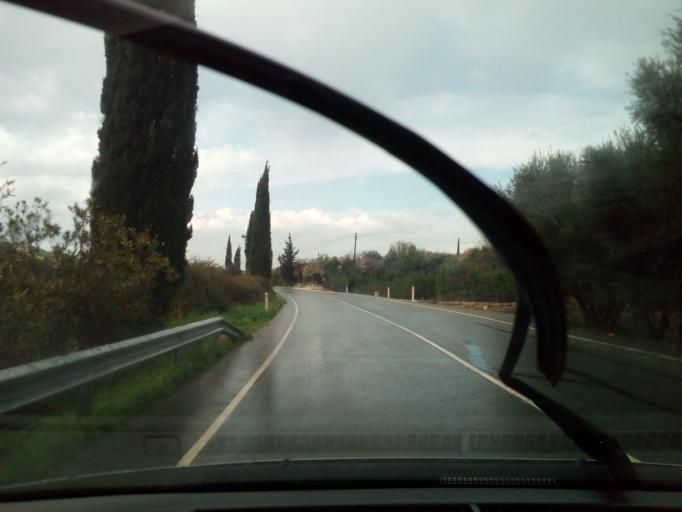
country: CY
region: Pafos
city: Polis
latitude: 35.0155
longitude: 32.4504
